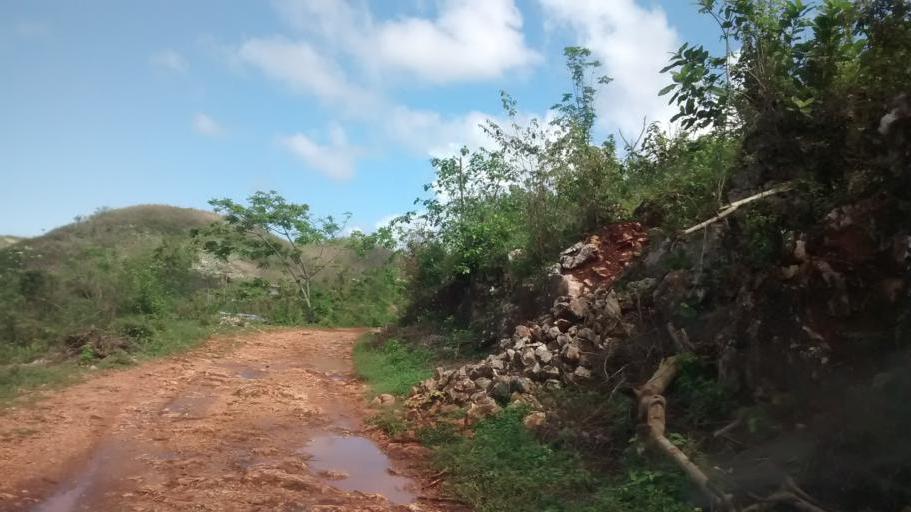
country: HT
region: Grandans
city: Corail
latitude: 18.5431
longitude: -73.9159
